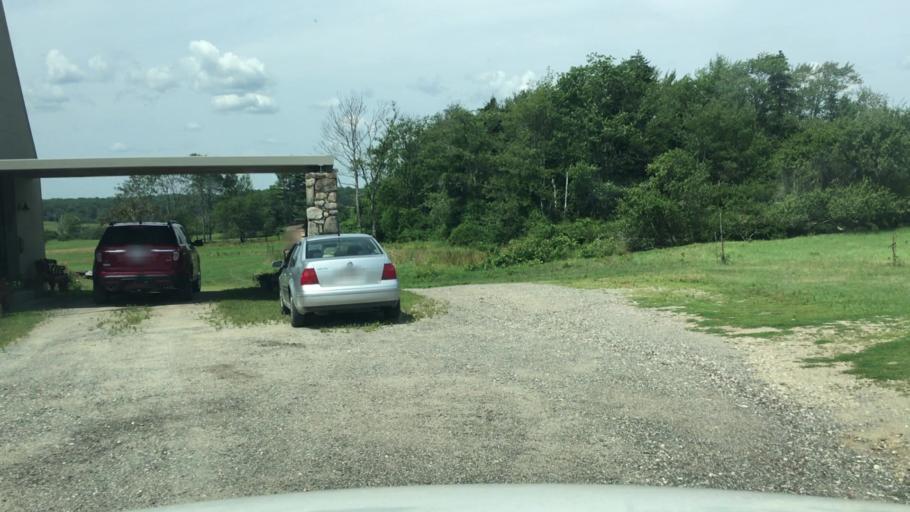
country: US
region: Maine
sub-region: Cumberland County
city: Scarborough
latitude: 43.5683
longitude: -70.2667
